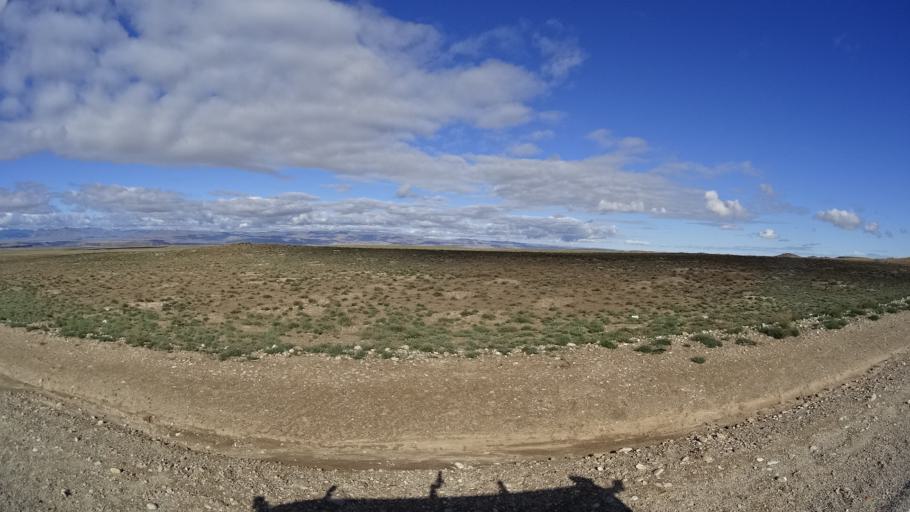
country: US
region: Idaho
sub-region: Ada County
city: Kuna
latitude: 43.3557
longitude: -116.4140
